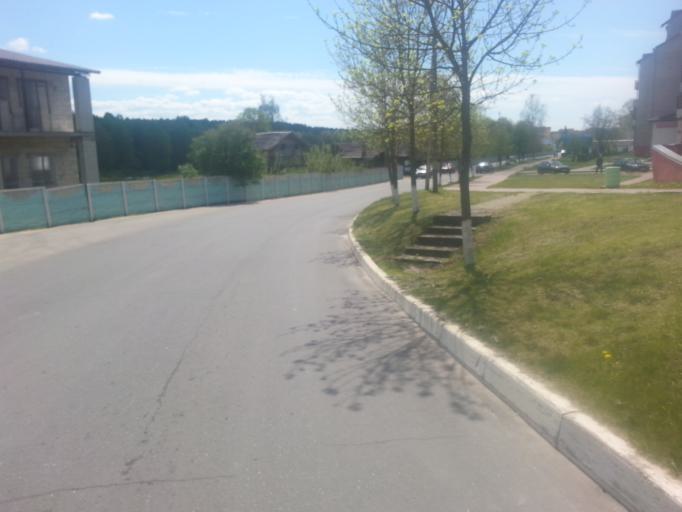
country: BY
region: Minsk
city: Narach
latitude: 54.9137
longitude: 26.7072
